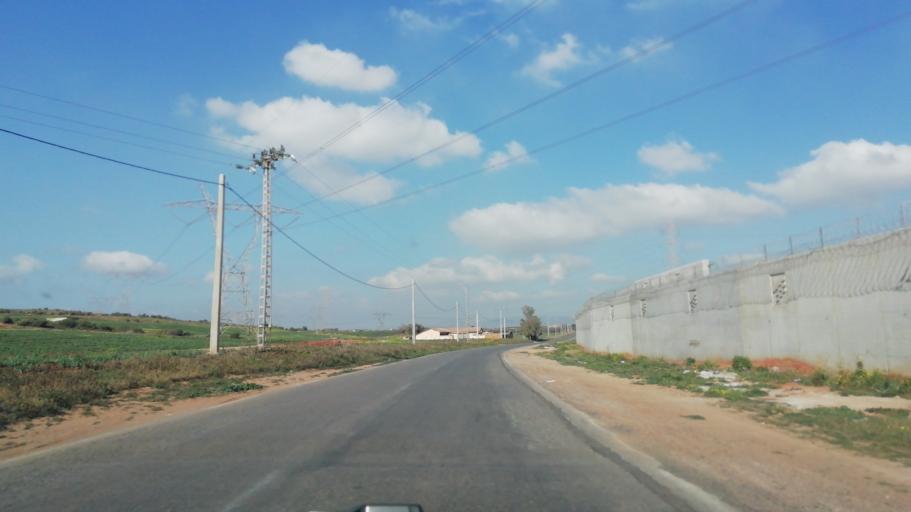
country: DZ
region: Oran
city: Ain el Bya
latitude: 35.7508
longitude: -0.2649
